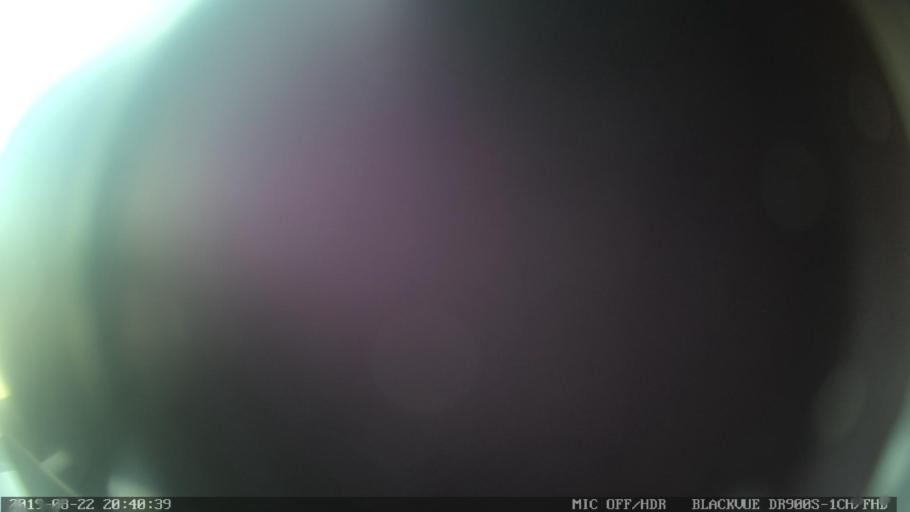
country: PT
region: Castelo Branco
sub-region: Proenca-A-Nova
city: Proenca-a-Nova
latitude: 39.6859
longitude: -7.7916
